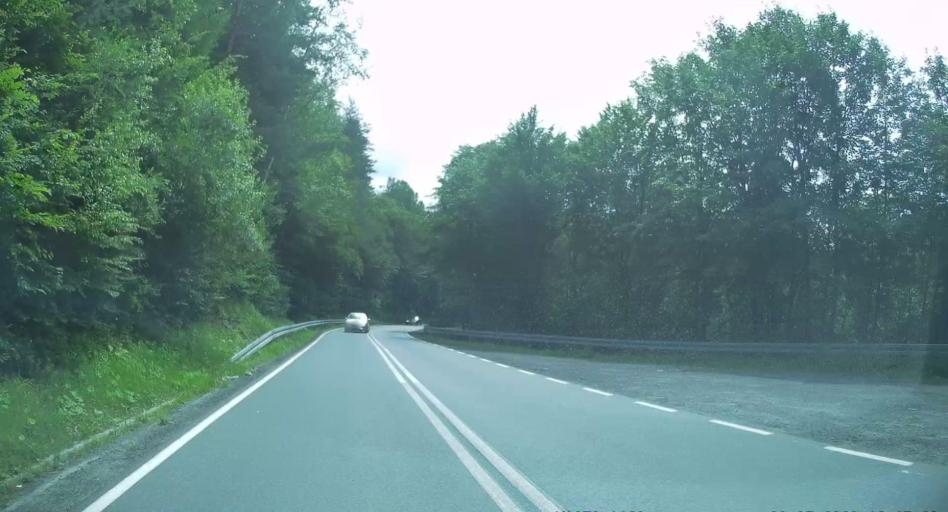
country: PL
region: Lesser Poland Voivodeship
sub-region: Powiat nowosadecki
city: Muszyna
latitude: 49.3496
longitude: 20.8025
